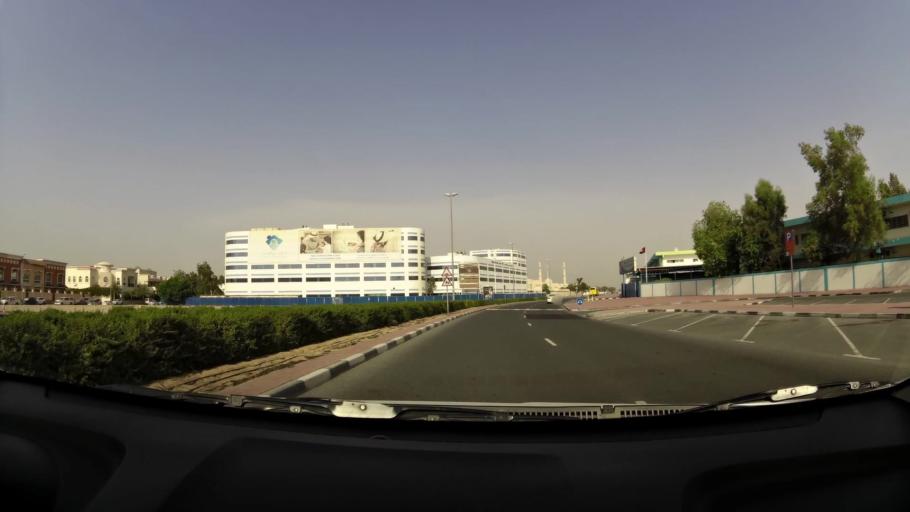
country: AE
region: Ash Shariqah
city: Sharjah
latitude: 25.2398
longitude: 55.3455
